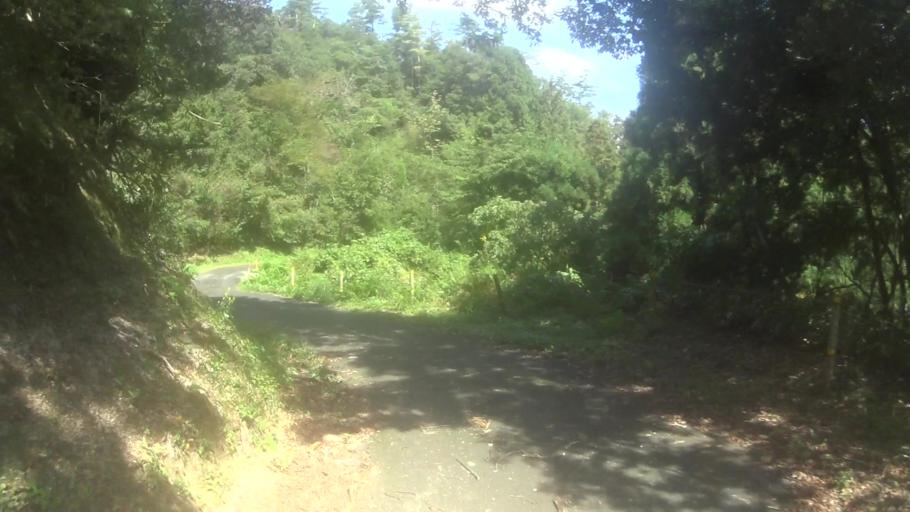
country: JP
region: Kyoto
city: Miyazu
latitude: 35.6694
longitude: 135.1407
